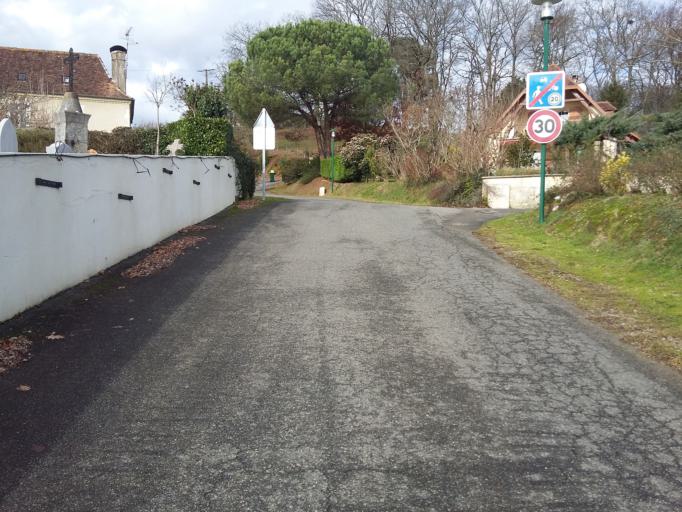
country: FR
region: Aquitaine
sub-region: Departement des Pyrenees-Atlantiques
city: Orthez
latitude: 43.4912
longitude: -0.6987
